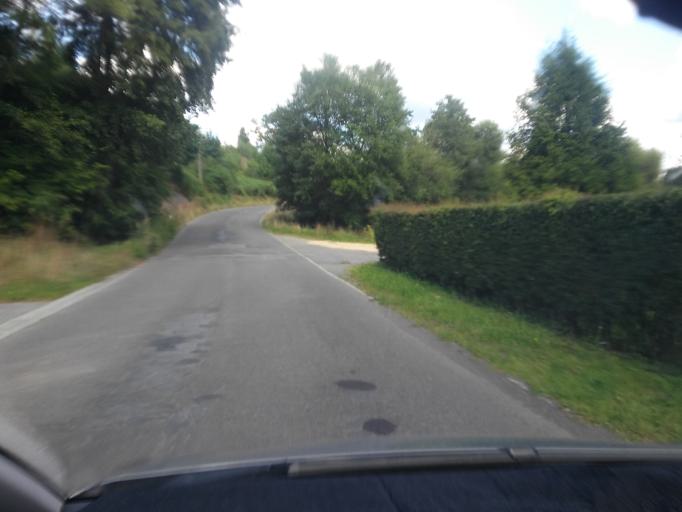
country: BE
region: Wallonia
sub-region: Province du Luxembourg
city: Saint-Hubert
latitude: 50.0291
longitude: 5.3069
